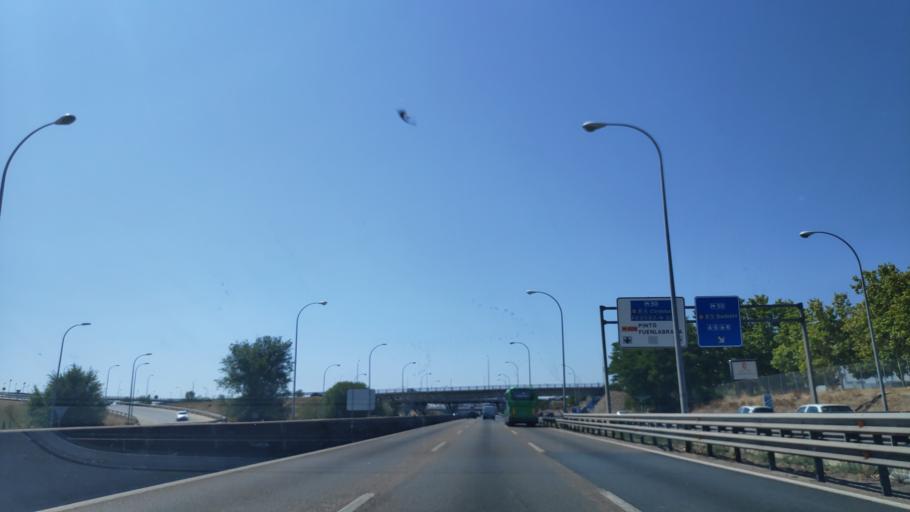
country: ES
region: Madrid
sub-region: Provincia de Madrid
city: Getafe
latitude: 40.2820
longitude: -3.7467
